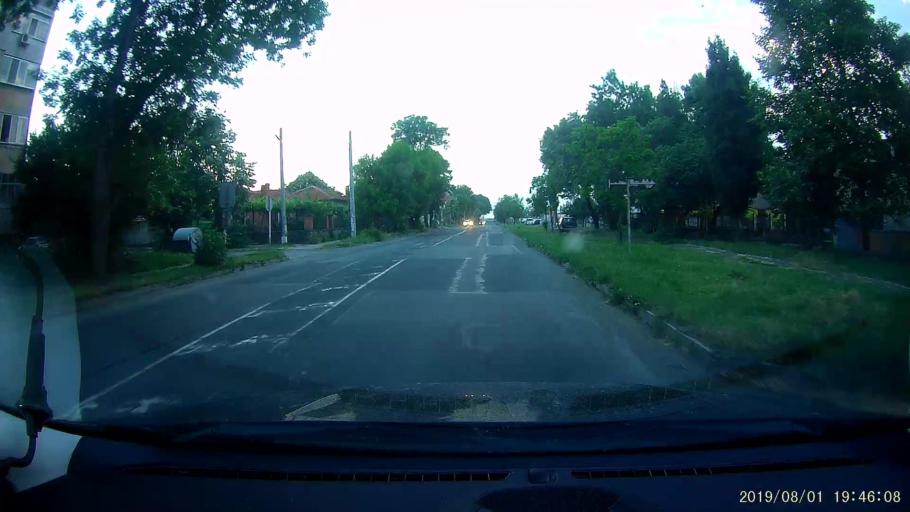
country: BG
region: Burgas
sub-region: Obshtina Karnobat
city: Karnobat
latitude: 42.6505
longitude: 26.9755
